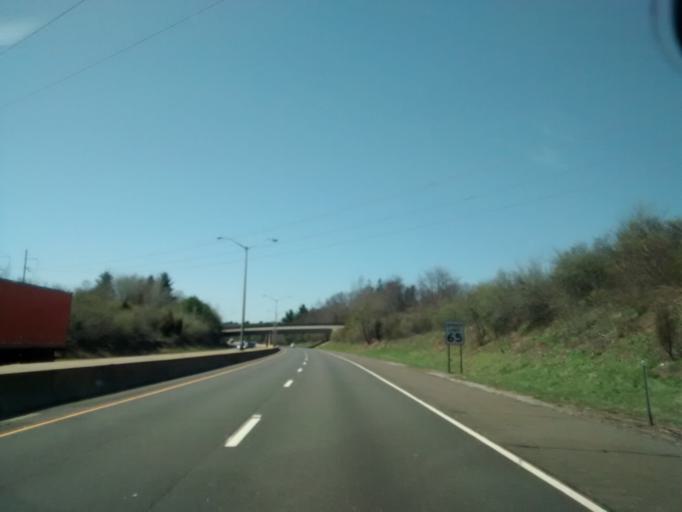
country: US
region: Connecticut
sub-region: Hartford County
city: East Hartford
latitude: 41.7992
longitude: -72.5798
